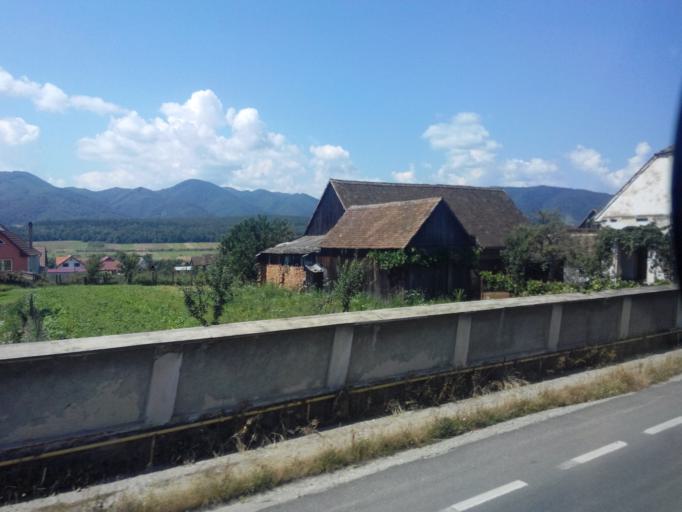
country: RO
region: Sibiu
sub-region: Comuna Orlat
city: Orlat
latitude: 45.7841
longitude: 23.9386
